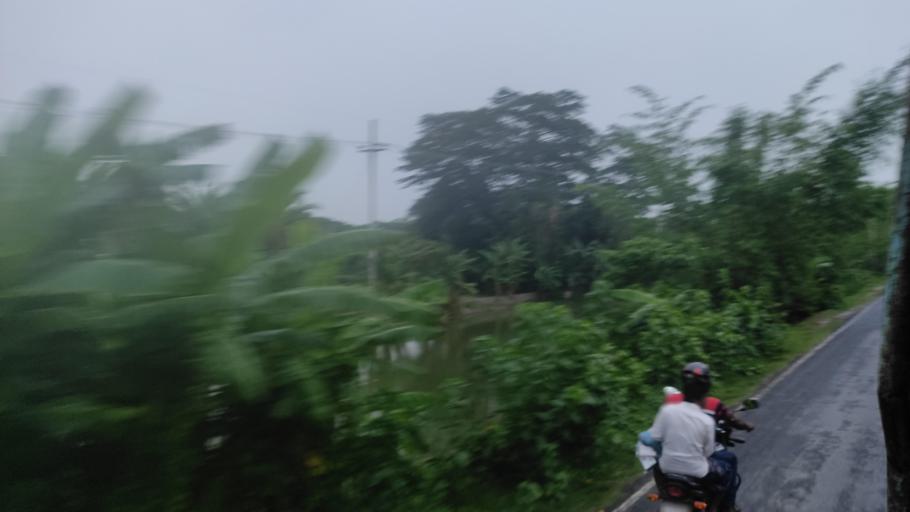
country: BD
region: Barisal
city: Bhandaria
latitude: 22.2972
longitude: 90.3247
